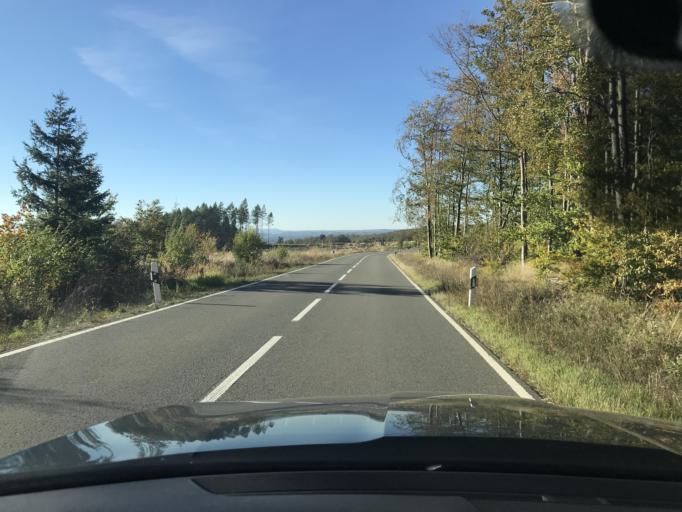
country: DE
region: Saxony-Anhalt
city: Friedrichsbrunn
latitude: 51.7041
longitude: 11.0246
